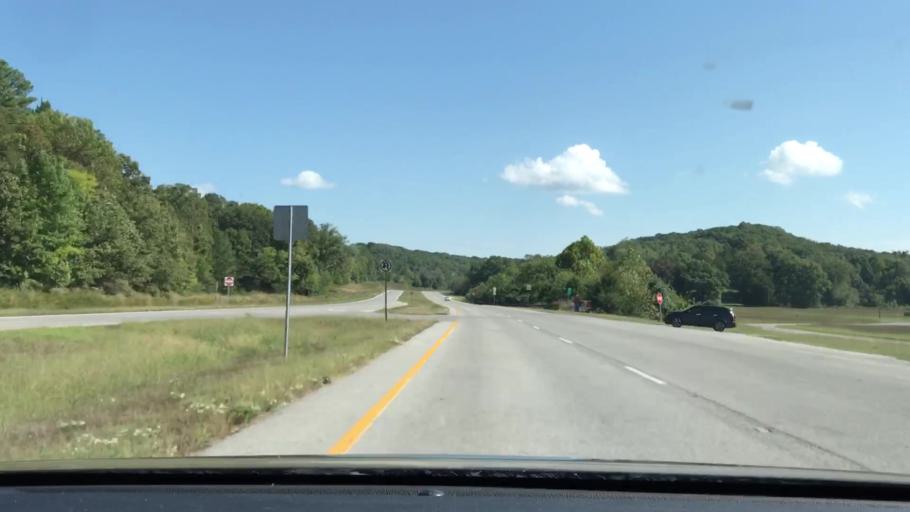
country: US
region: Kentucky
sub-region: Marshall County
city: Benton
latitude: 36.7756
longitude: -88.1050
